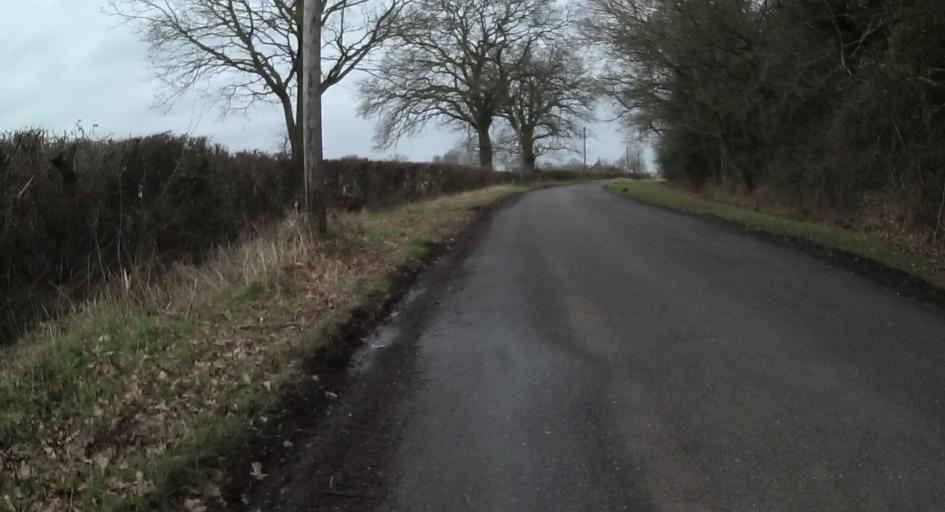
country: GB
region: England
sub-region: West Berkshire
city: Stratfield Mortimer
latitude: 51.3752
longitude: -1.0400
